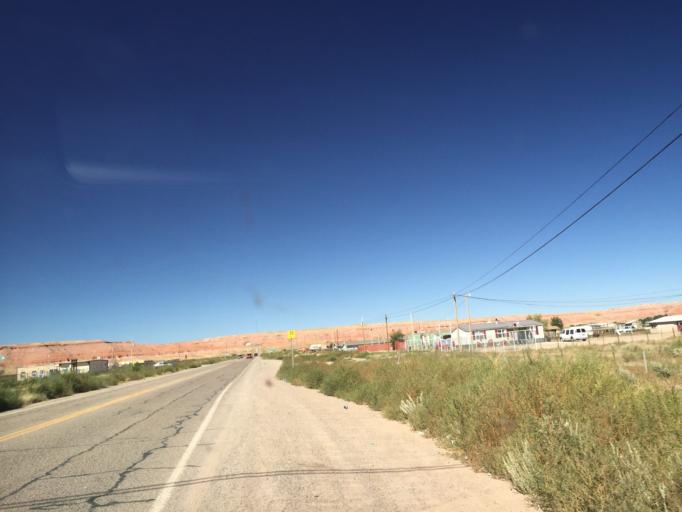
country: US
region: Arizona
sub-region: Apache County
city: Many Farms
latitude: 36.3542
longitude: -109.6184
